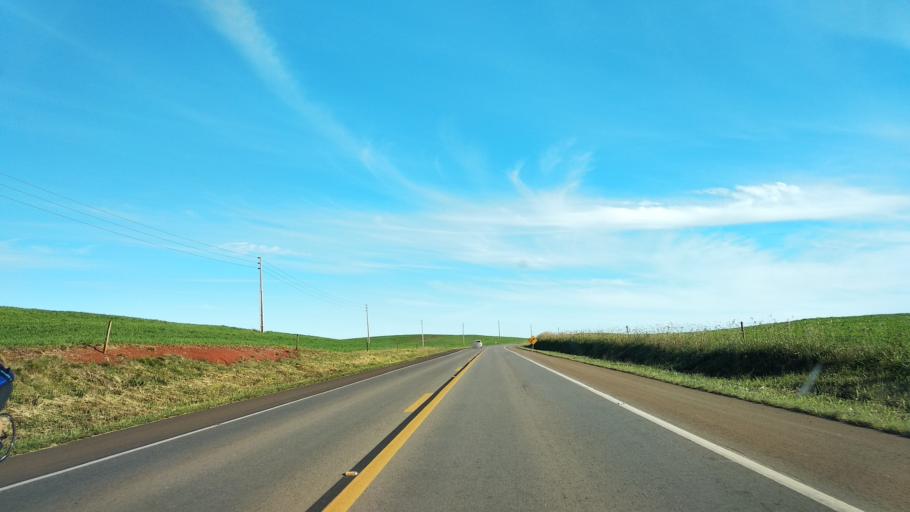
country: BR
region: Santa Catarina
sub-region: Celso Ramos
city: Celso Ramos
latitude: -27.5196
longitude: -51.3514
